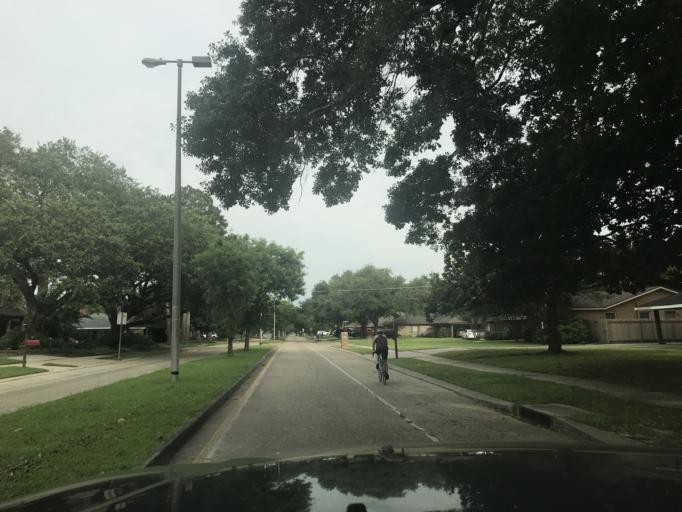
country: US
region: Louisiana
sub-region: Lafayette Parish
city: Lafayette
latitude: 30.1974
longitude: -92.0486
